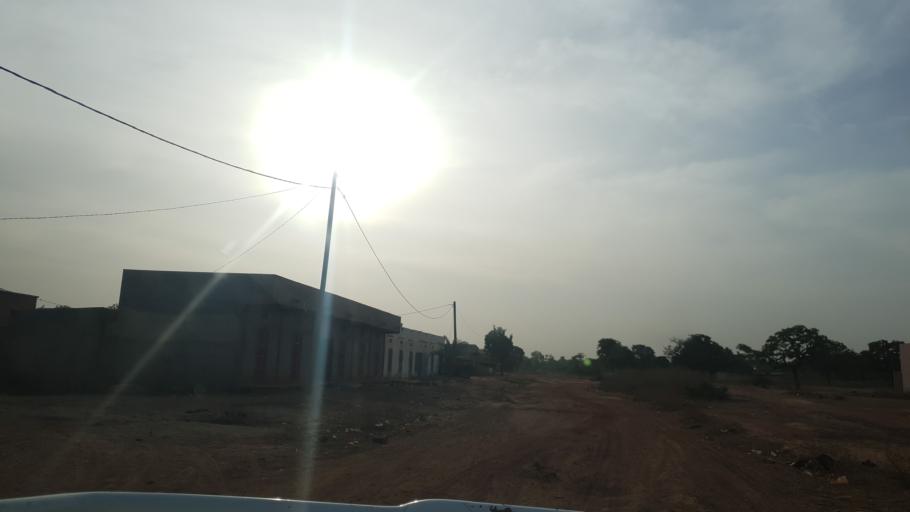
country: ML
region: Segou
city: Baroueli
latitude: 12.7738
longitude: -6.9368
